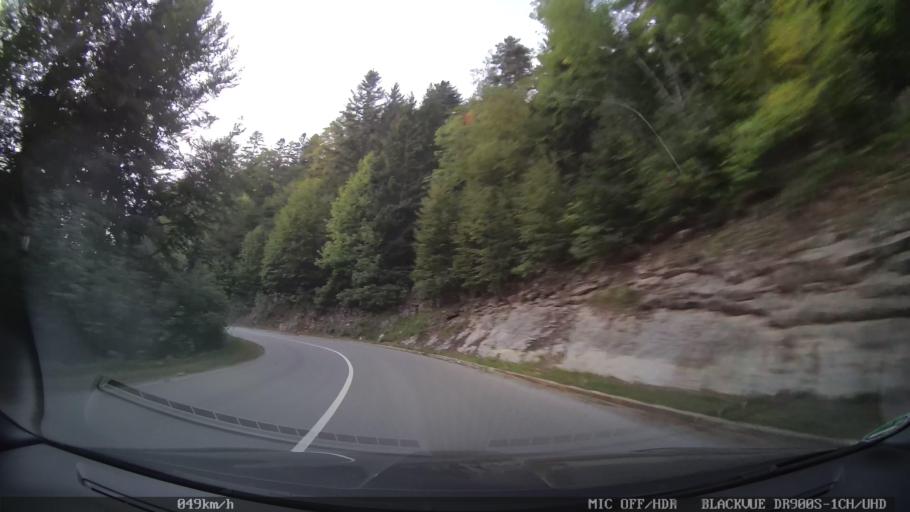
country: HR
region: Primorsko-Goranska
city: Novi Vinodolski
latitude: 45.1838
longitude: 14.9268
